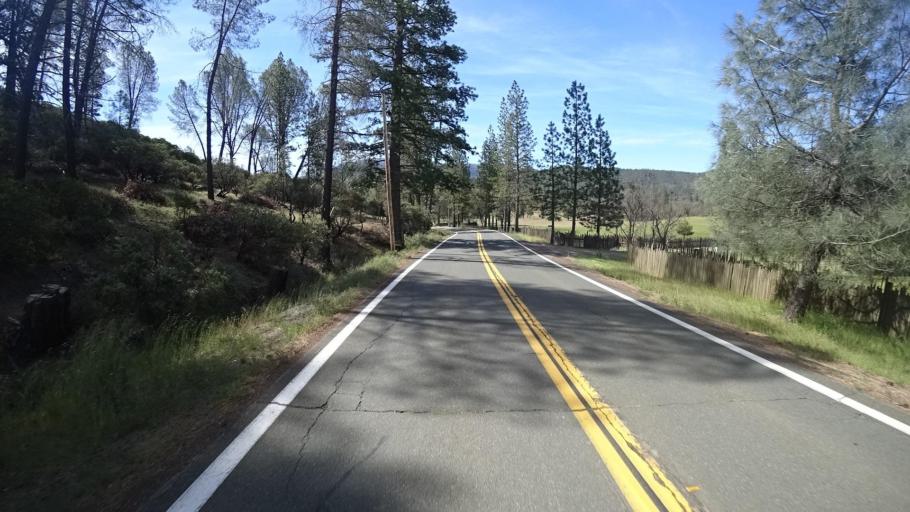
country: US
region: California
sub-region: Lake County
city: Cobb
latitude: 38.8638
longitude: -122.7648
